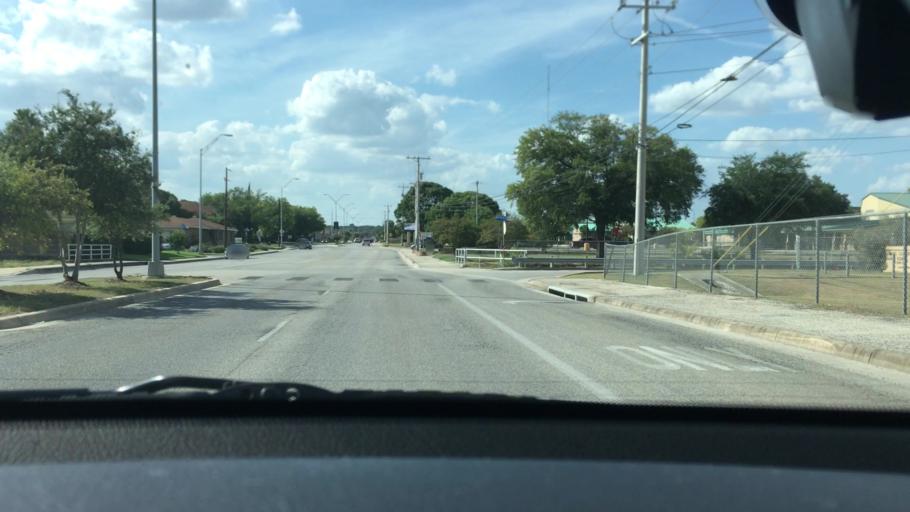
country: US
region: Texas
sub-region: Guadalupe County
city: Schertz
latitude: 29.5631
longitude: -98.2688
